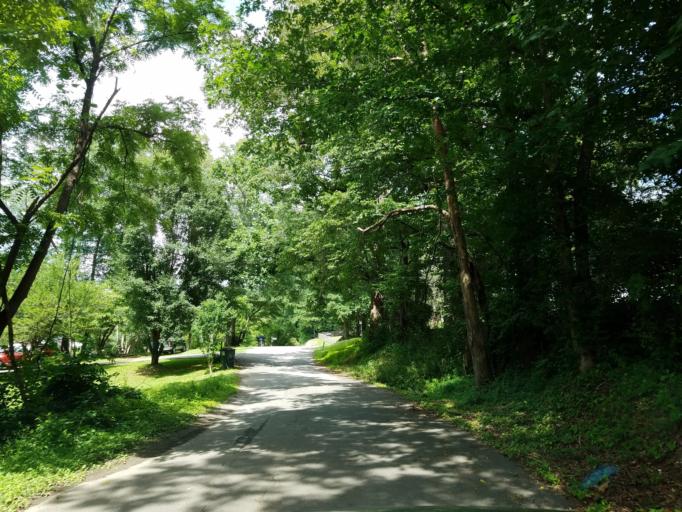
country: US
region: Georgia
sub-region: Cherokee County
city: Ball Ground
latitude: 34.3324
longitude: -84.3796
